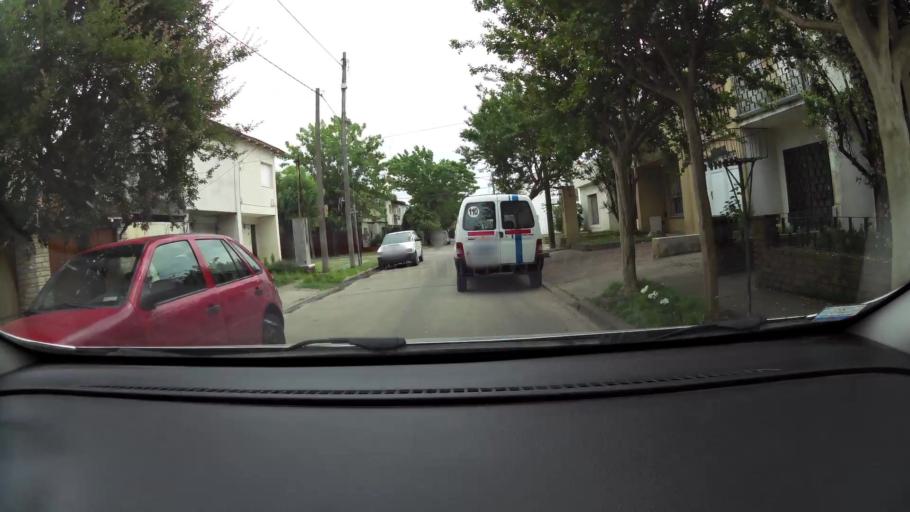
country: AR
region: Buenos Aires
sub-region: Partido de Campana
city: Campana
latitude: -34.1756
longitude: -58.9657
